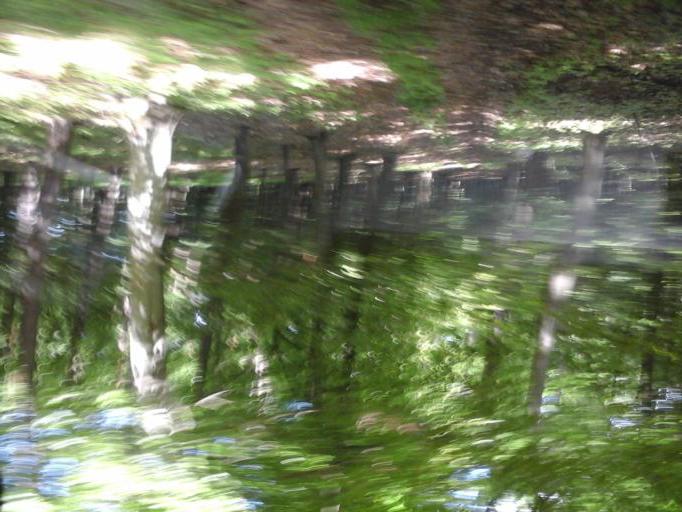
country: PL
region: West Pomeranian Voivodeship
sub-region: Powiat choszczenski
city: Bierzwnik
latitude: 53.0692
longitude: 15.6602
